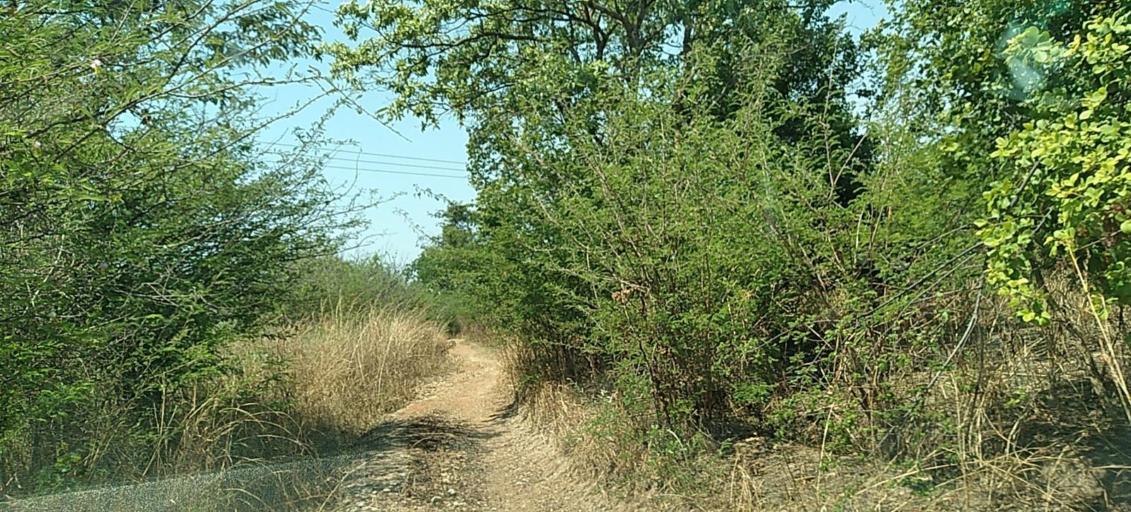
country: ZM
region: Copperbelt
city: Luanshya
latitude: -12.9895
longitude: 28.3257
